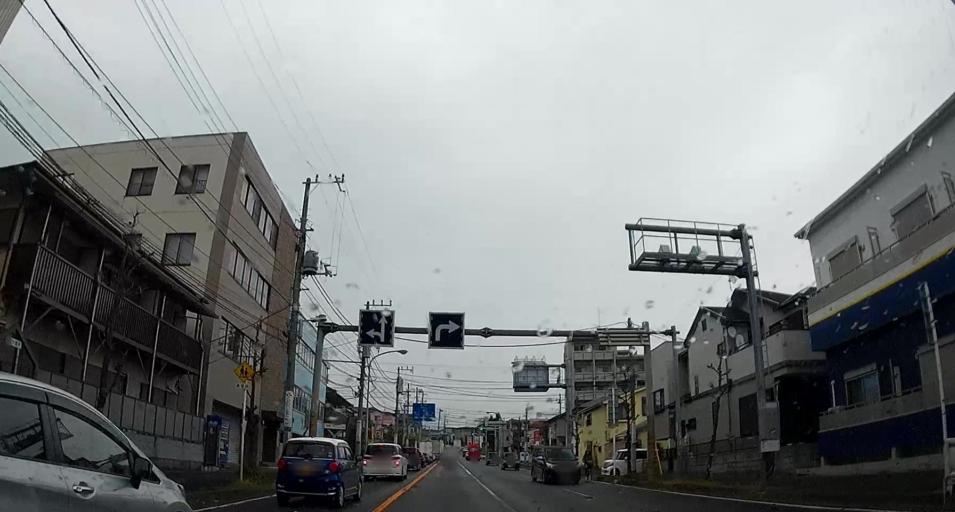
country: JP
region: Chiba
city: Funabashi
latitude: 35.7102
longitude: 139.9547
